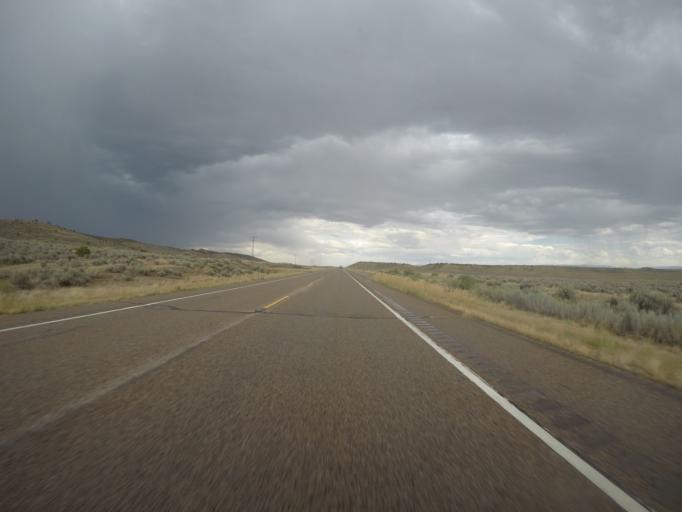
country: US
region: Colorado
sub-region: Rio Blanco County
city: Rangely
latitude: 40.2419
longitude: -108.9422
